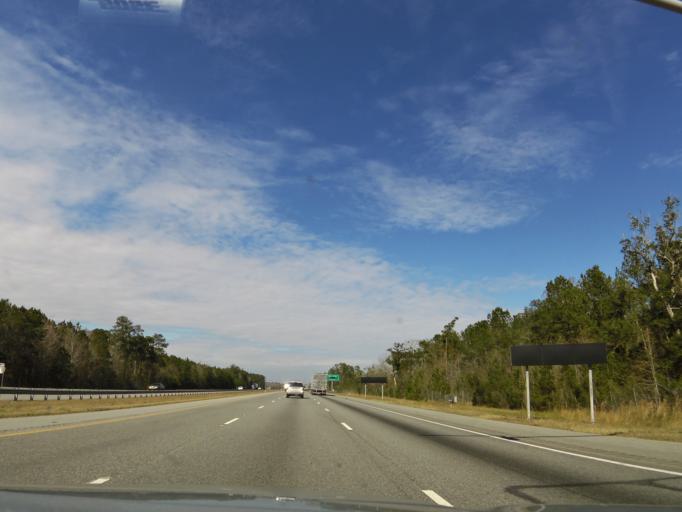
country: US
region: Georgia
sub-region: McIntosh County
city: Darien
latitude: 31.4667
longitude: -81.4465
